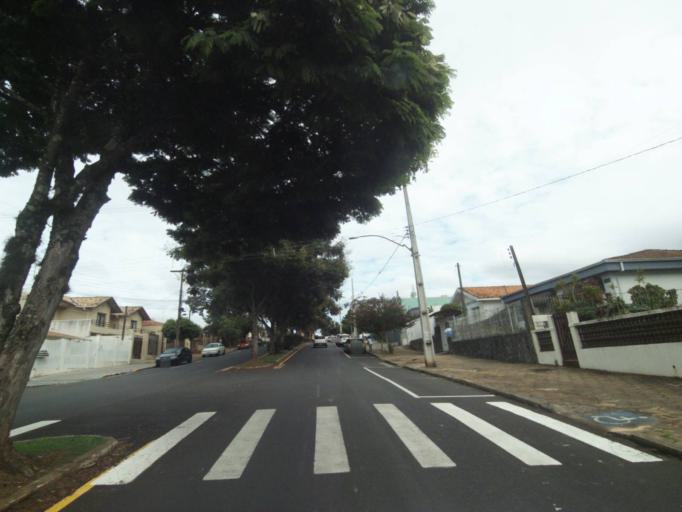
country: BR
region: Parana
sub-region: Telemaco Borba
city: Telemaco Borba
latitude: -24.3312
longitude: -50.6180
